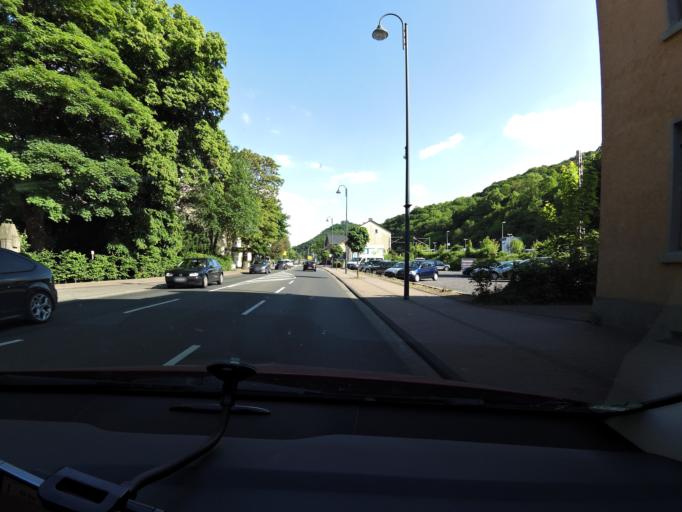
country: DE
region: Rheinland-Pfalz
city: Bad Honningen
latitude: 50.5053
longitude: 7.3038
